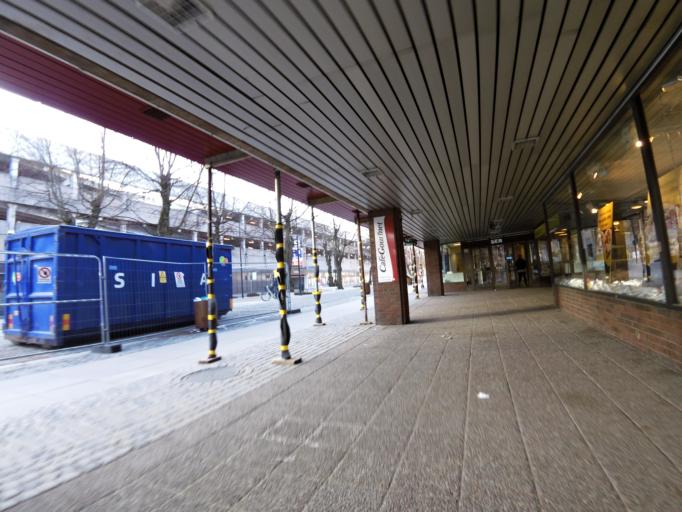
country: SE
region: Gaevleborg
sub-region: Gavle Kommun
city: Gavle
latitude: 60.6748
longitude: 17.1399
